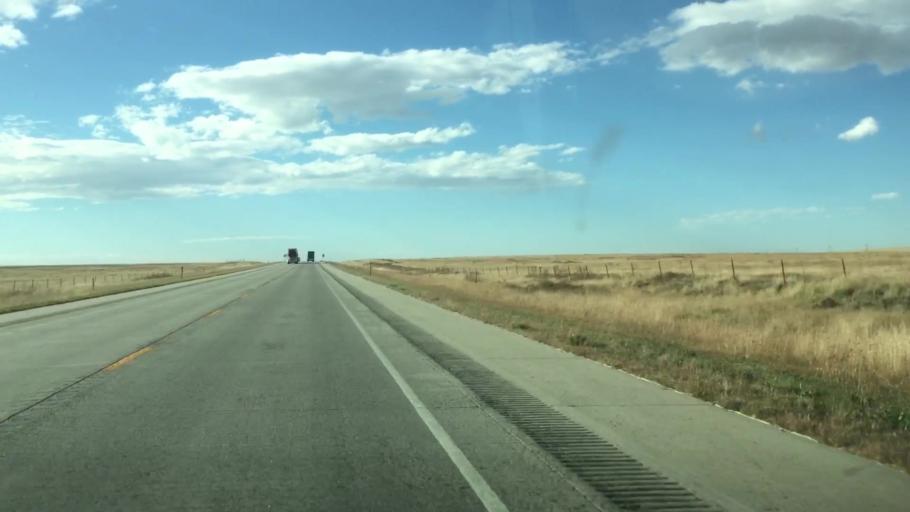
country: US
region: Colorado
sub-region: Lincoln County
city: Hugo
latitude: 39.1844
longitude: -103.5521
